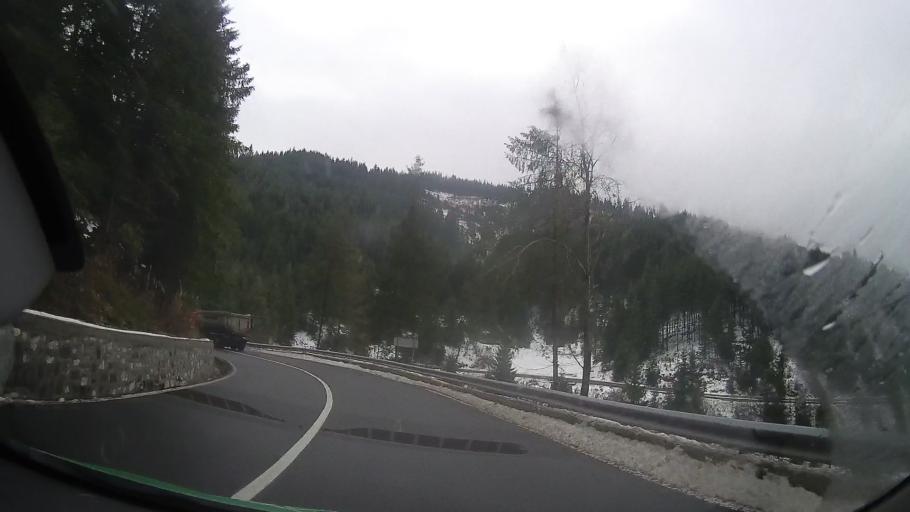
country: RO
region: Harghita
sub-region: Municipiul Gheorgheni
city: Gheorgheni
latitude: 46.7700
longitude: 25.7103
